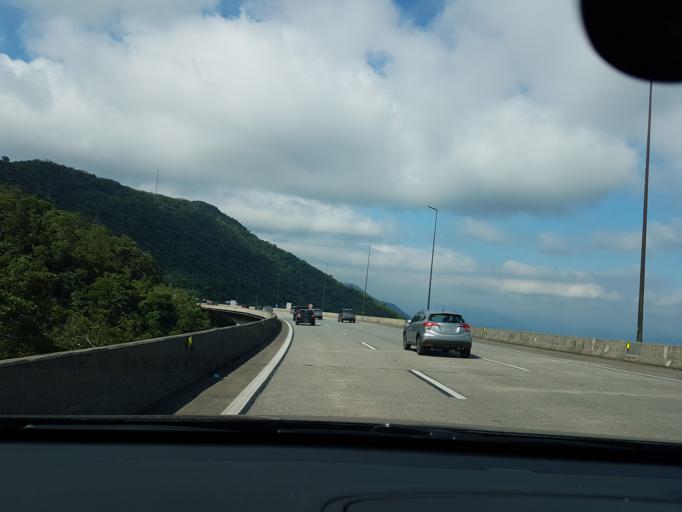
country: BR
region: Sao Paulo
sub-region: Cubatao
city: Cubatao
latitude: -23.9237
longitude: -46.5332
